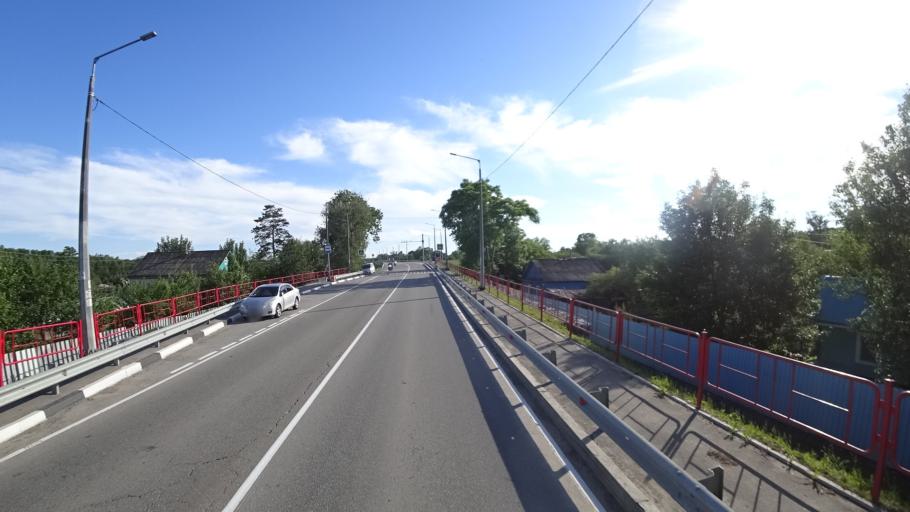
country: RU
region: Khabarovsk Krai
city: Khor
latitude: 47.8867
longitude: 134.9751
